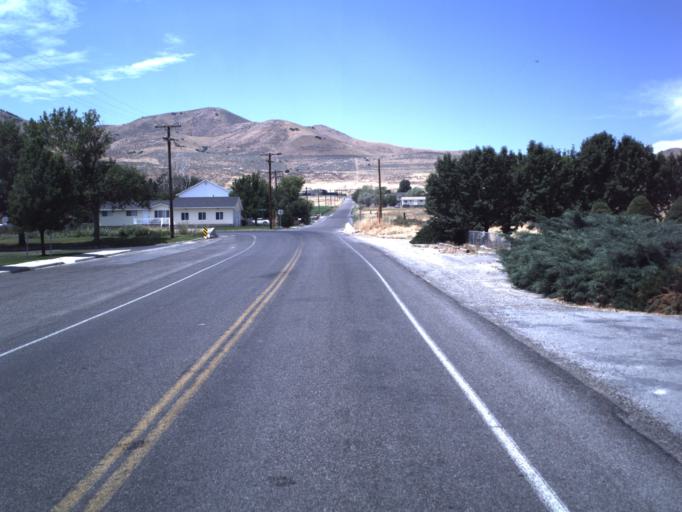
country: US
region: Utah
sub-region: Box Elder County
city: Tremonton
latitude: 41.6944
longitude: -112.2934
